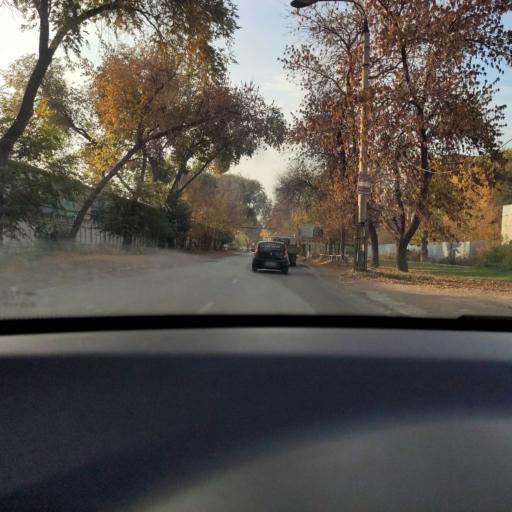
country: RU
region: Samara
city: Samara
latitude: 53.1908
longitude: 50.2452
